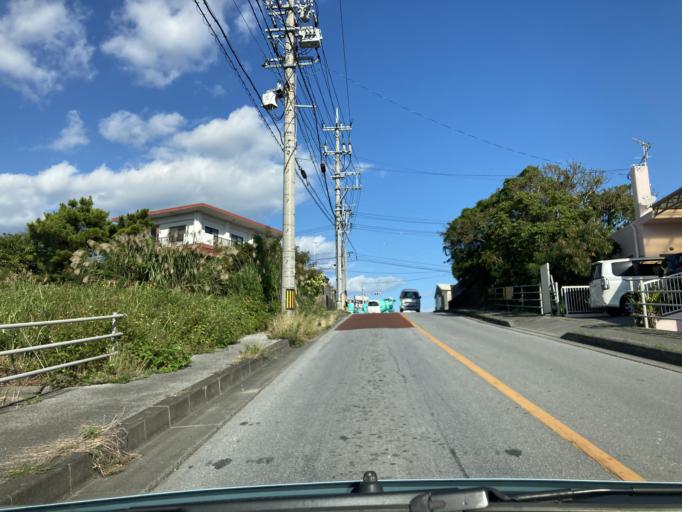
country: JP
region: Okinawa
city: Ginowan
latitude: 26.2167
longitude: 127.7415
